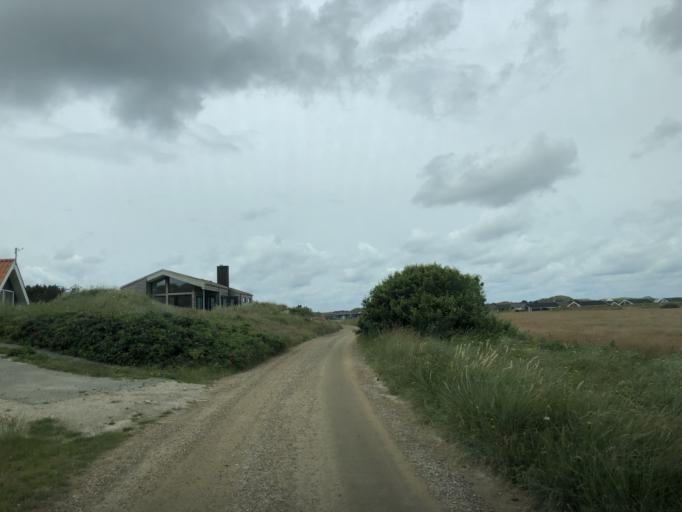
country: DK
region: Central Jutland
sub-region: Ringkobing-Skjern Kommune
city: Hvide Sande
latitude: 55.9245
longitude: 8.1655
